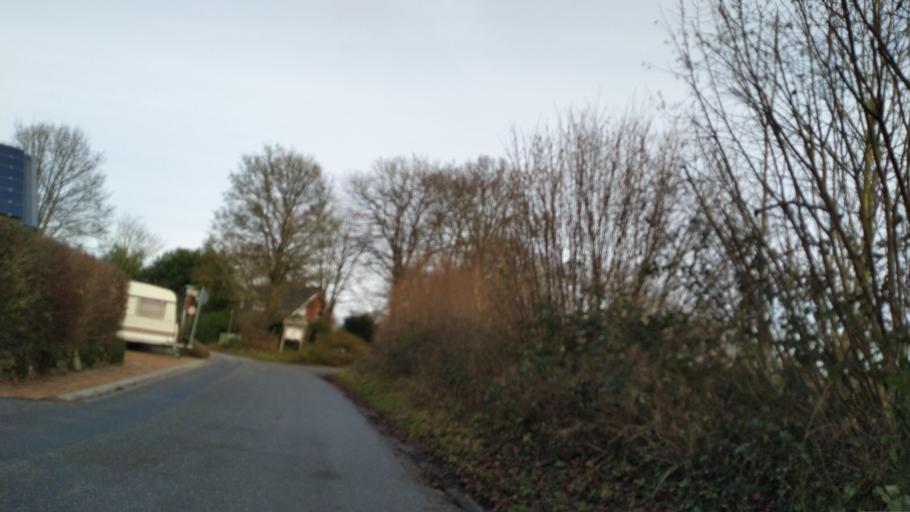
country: DE
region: Schleswig-Holstein
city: Eutin
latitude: 54.1917
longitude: 10.6082
